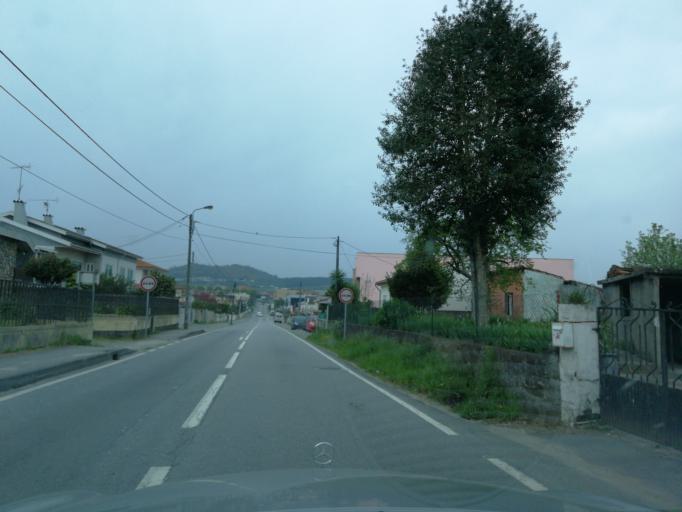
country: PT
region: Braga
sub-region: Braga
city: Braga
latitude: 41.5637
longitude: -8.4419
